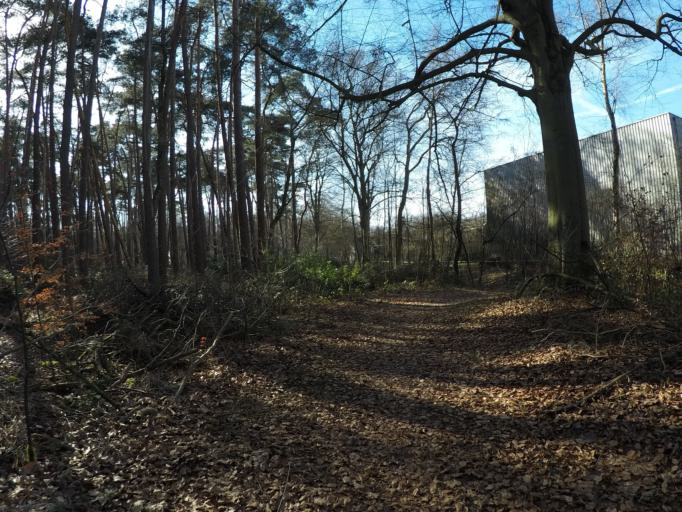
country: BE
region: Flanders
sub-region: Provincie Antwerpen
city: Wijnegem
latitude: 51.2336
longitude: 4.5465
